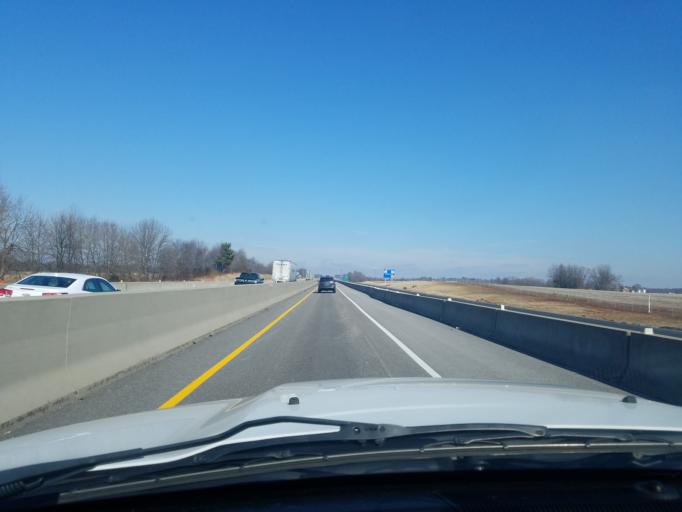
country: US
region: Kentucky
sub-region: Hardin County
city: Elizabethtown
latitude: 37.5779
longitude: -85.8726
